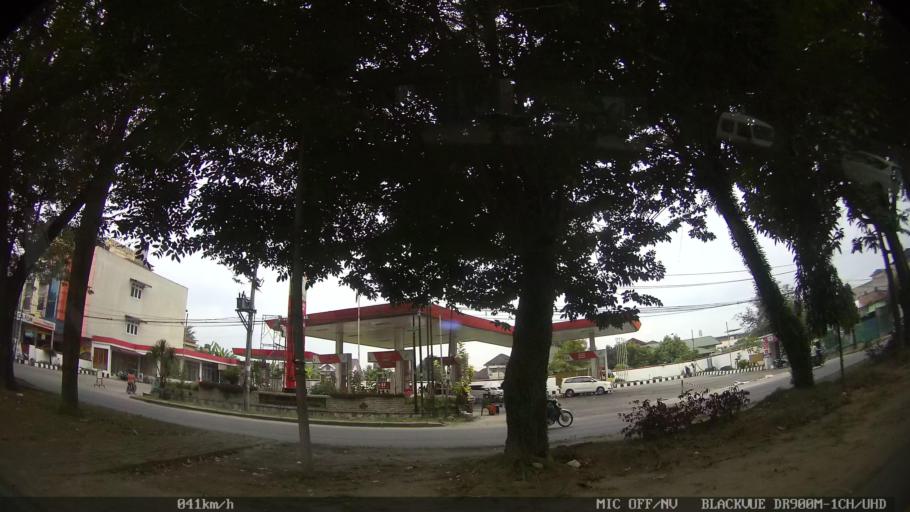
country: ID
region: North Sumatra
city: Deli Tua
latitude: 3.5382
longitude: 98.6881
